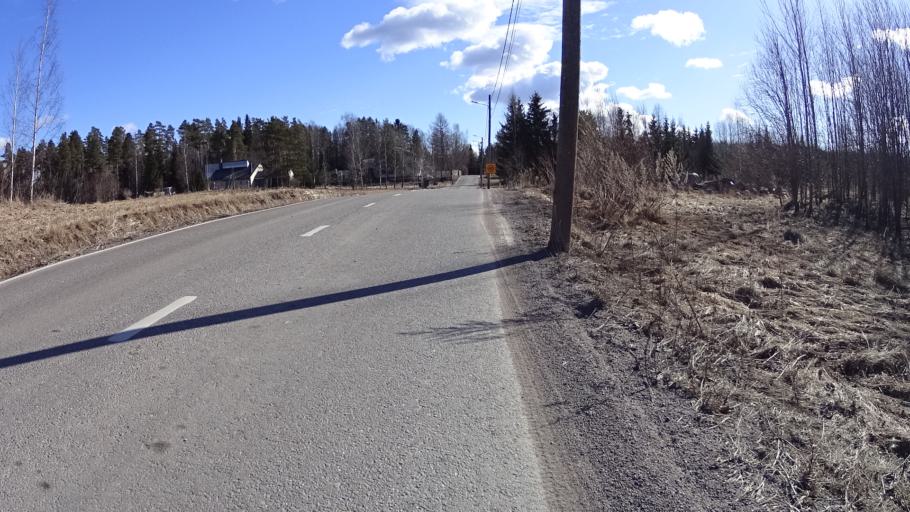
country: FI
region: Uusimaa
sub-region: Helsinki
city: Kauniainen
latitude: 60.2753
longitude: 24.7153
